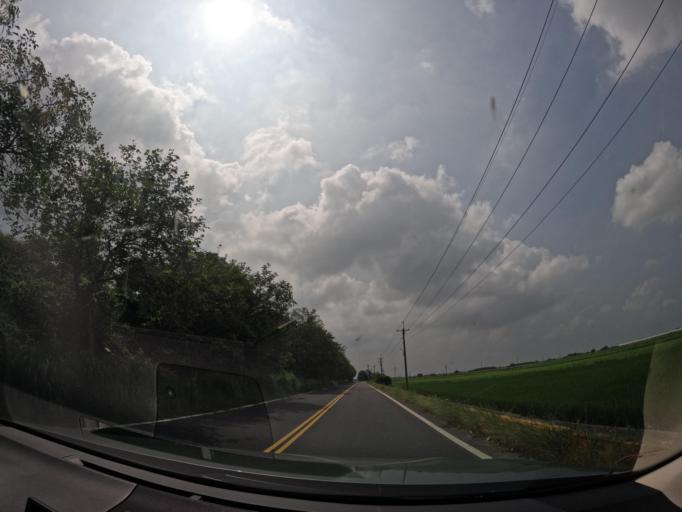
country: TW
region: Taiwan
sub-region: Chiayi
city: Jiayi Shi
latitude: 23.6136
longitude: 120.3667
